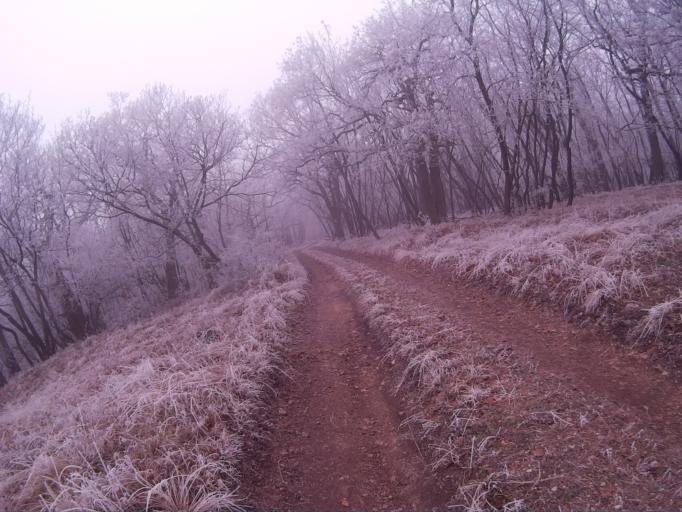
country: HU
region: Komarom-Esztergom
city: Oroszlany
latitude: 47.3931
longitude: 18.3327
